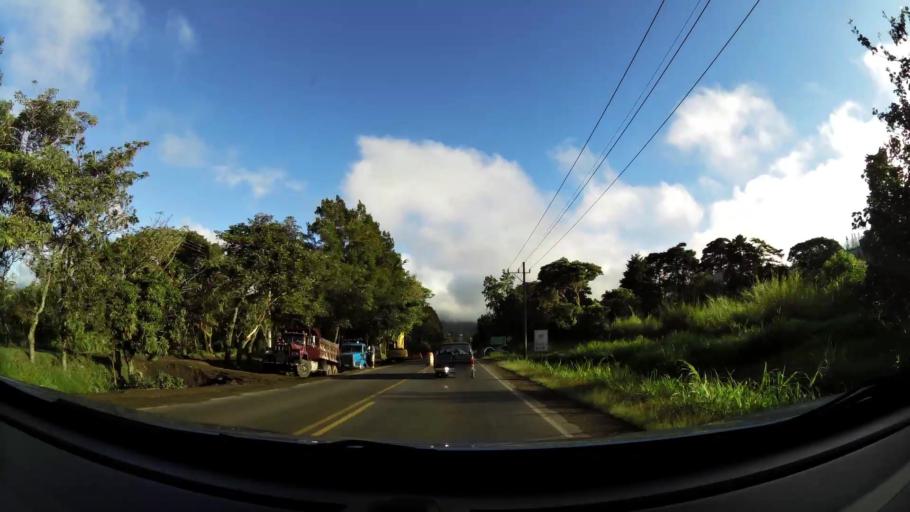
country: CR
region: Heredia
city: Angeles
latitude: 10.0091
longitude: -84.0312
